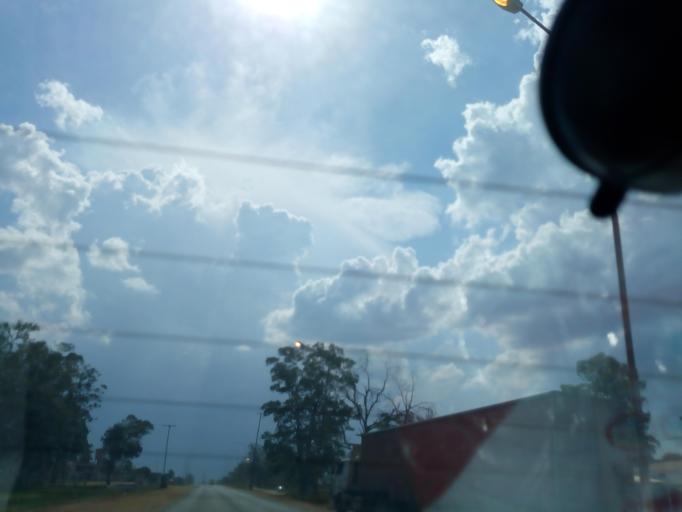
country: AR
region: Corrientes
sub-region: Departamento de Paso de los Libres
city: Paso de los Libres
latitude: -29.7218
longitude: -57.1271
